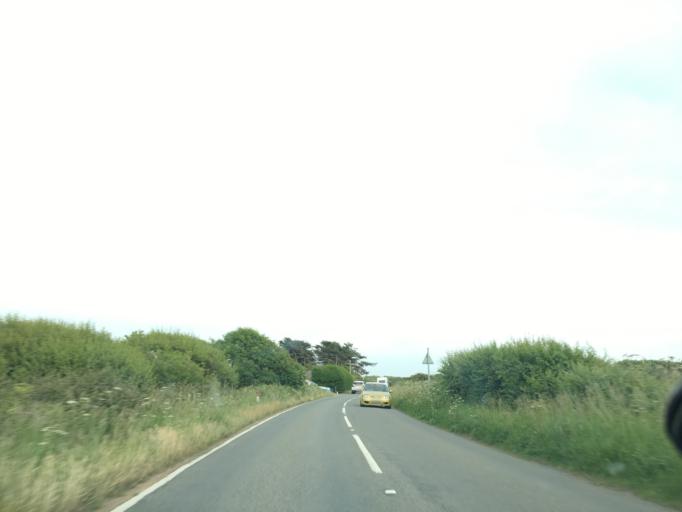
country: GB
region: England
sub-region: Isle of Wight
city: Shalfleet
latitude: 50.6471
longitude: -1.4445
